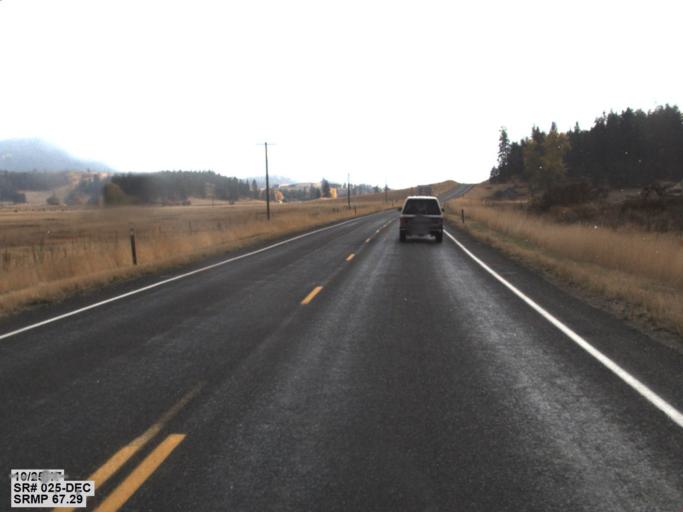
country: US
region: Washington
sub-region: Stevens County
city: Kettle Falls
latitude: 48.4427
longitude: -118.1705
